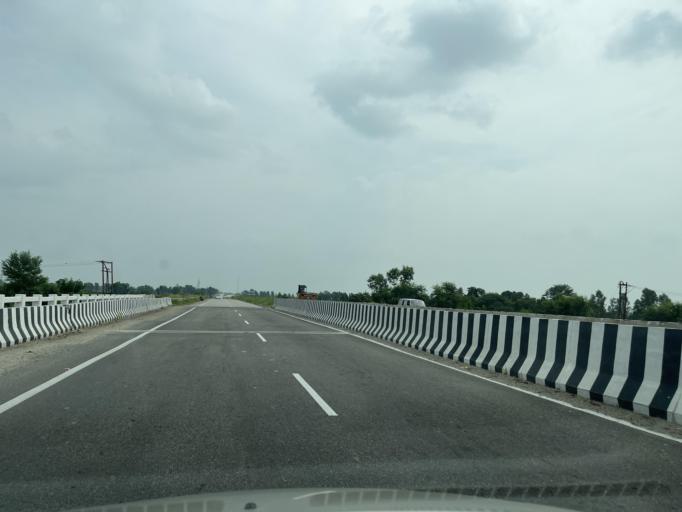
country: IN
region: Uttarakhand
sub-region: Udham Singh Nagar
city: Kashipur
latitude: 29.1985
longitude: 78.9346
